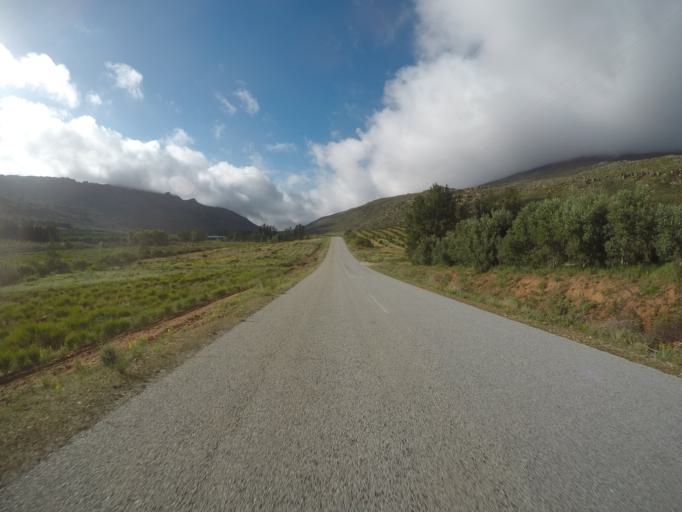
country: ZA
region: Western Cape
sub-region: West Coast District Municipality
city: Clanwilliam
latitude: -32.3601
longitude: 18.8544
